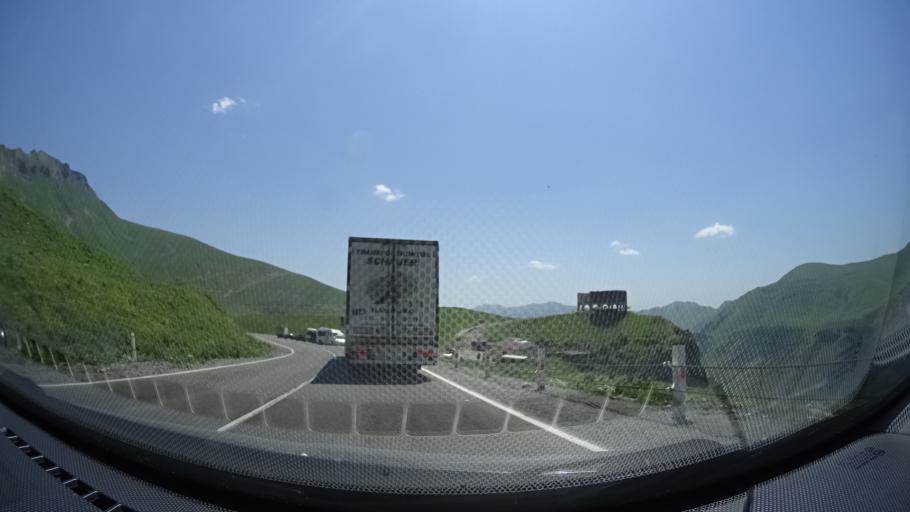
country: GE
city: Gudauri
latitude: 42.4945
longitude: 44.4516
